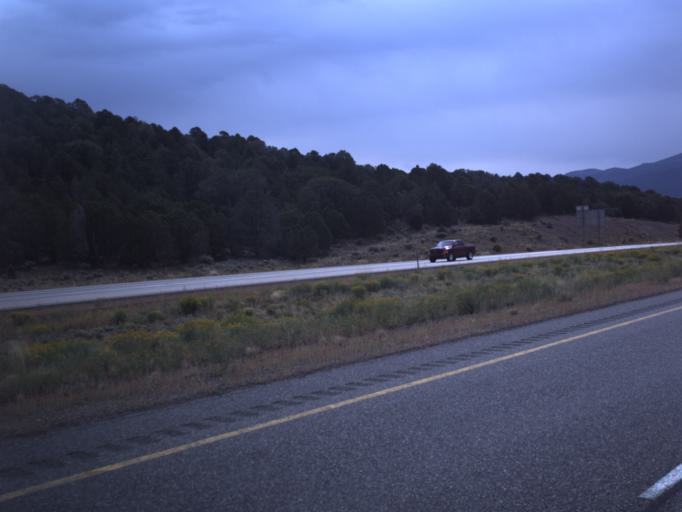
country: US
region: Utah
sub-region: Beaver County
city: Beaver
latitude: 38.5852
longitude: -112.4876
